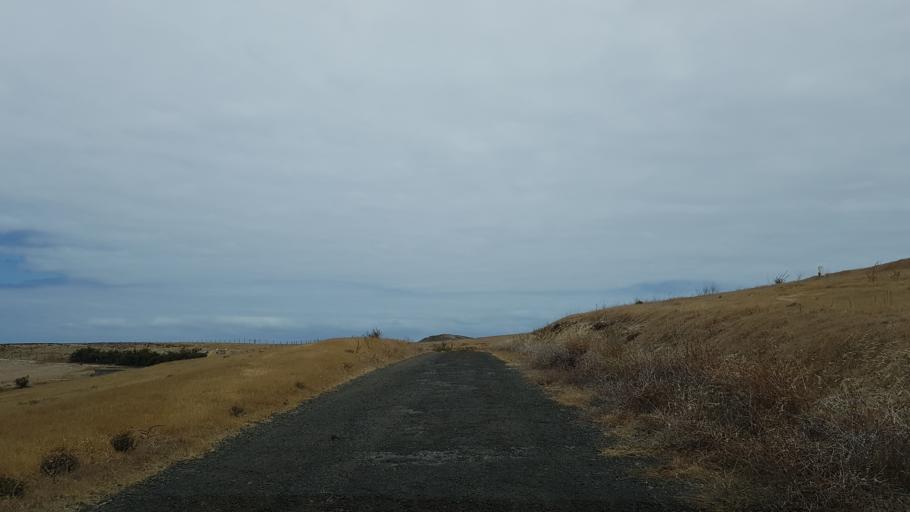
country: PT
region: Madeira
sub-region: Porto Santo
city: Camacha
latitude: 33.0908
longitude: -16.3361
